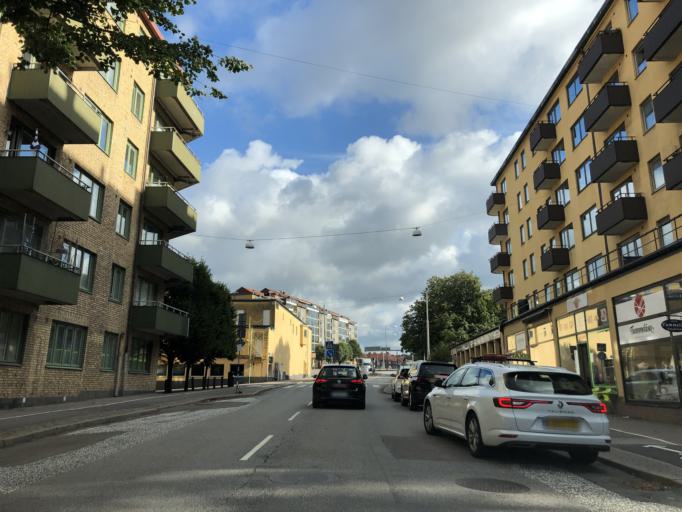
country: SE
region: Vaestra Goetaland
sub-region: Goteborg
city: Goeteborg
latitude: 57.7138
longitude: 12.0007
